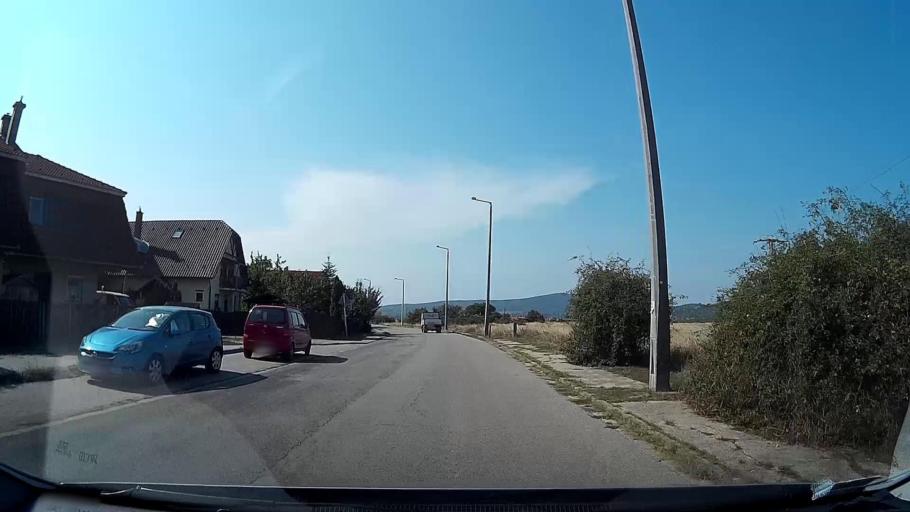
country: HU
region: Pest
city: Szentendre
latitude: 47.6730
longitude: 19.0539
